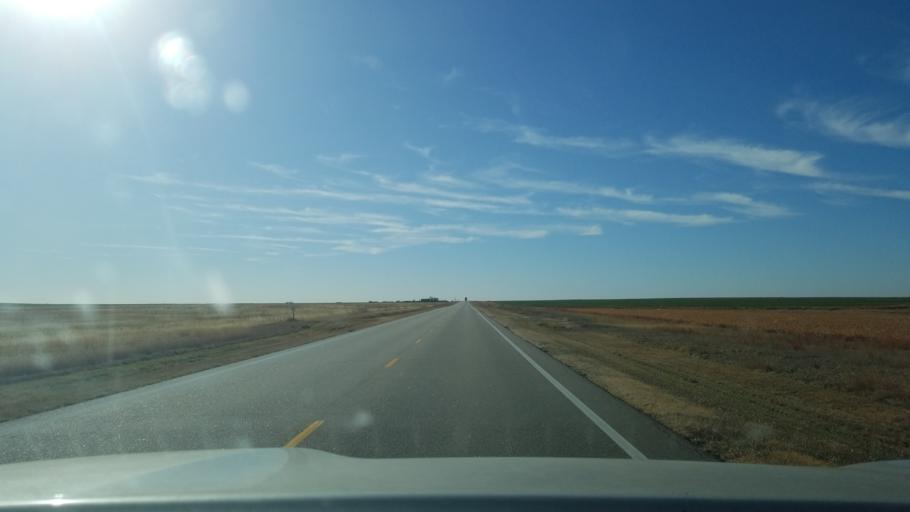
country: US
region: Kansas
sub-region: Ness County
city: Ness City
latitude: 38.3438
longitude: -99.8979
